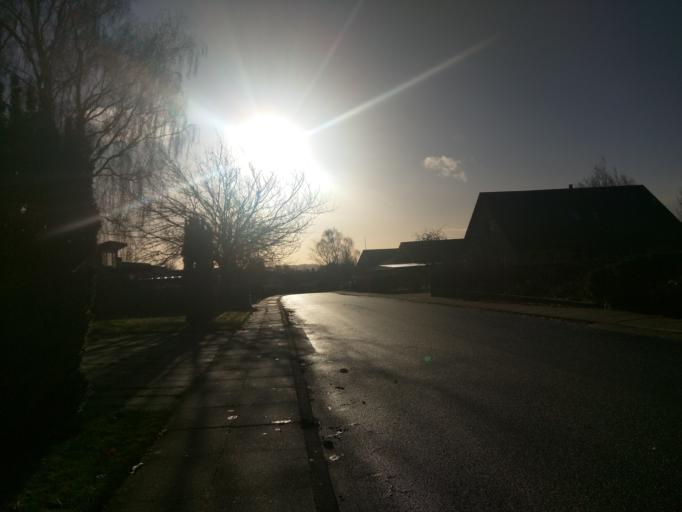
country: DK
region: Central Jutland
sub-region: Silkeborg Kommune
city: Silkeborg
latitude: 56.1857
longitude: 9.5243
